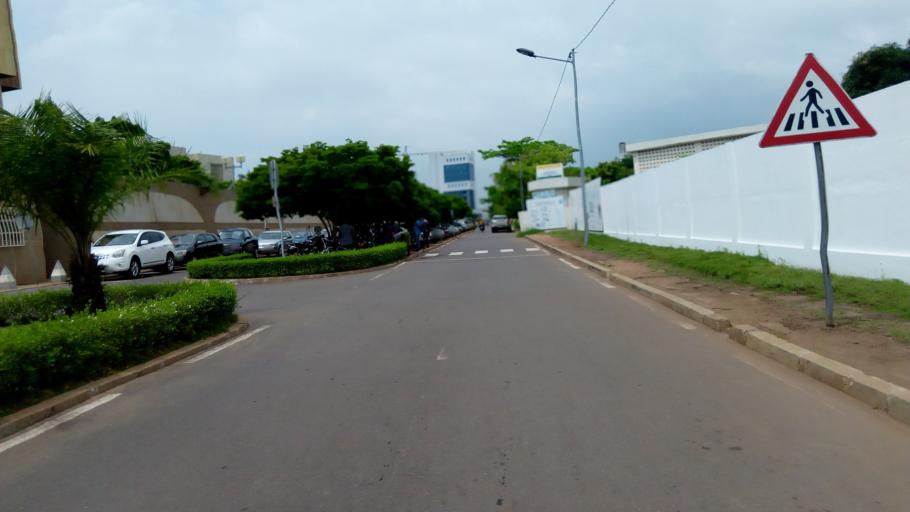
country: TG
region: Maritime
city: Lome
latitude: 6.1282
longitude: 1.2129
